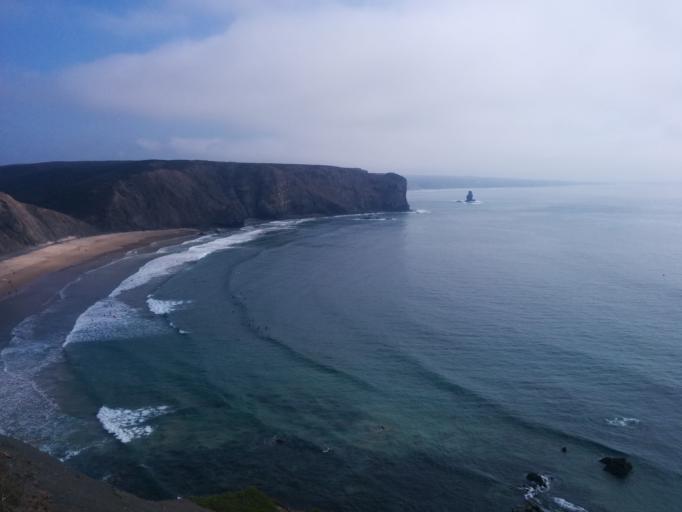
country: PT
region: Faro
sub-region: Aljezur
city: Aljezur
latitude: 37.2961
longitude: -8.8685
